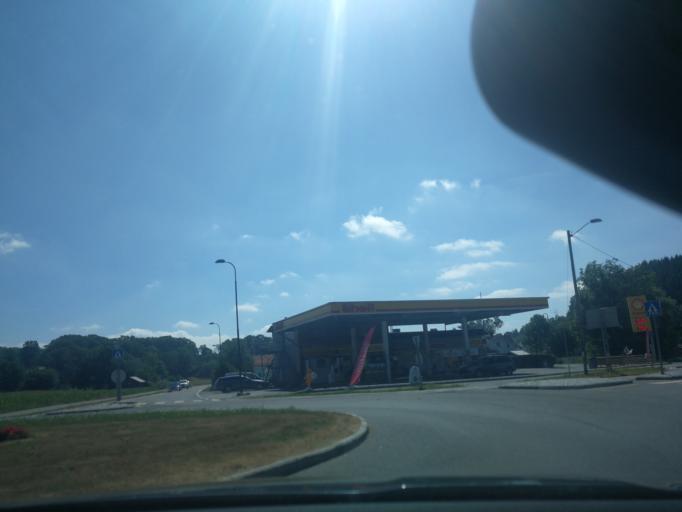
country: NO
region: Vestfold
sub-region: Stokke
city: Melsomvik
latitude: 59.2247
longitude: 10.3361
